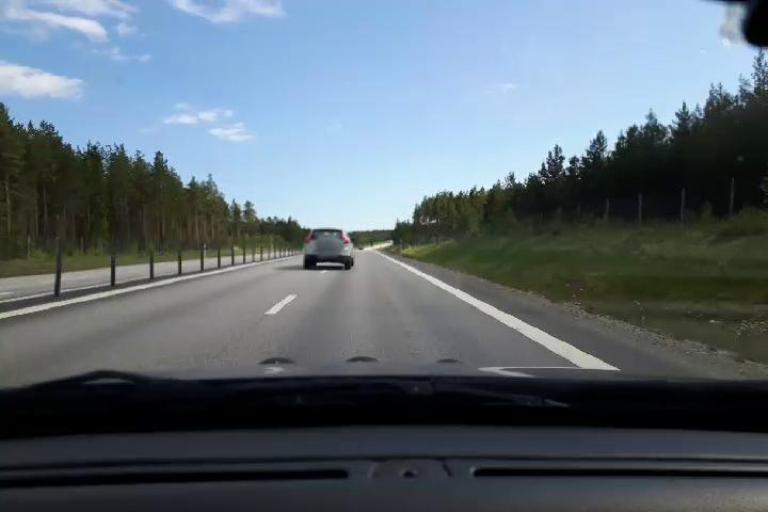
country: SE
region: Gaevleborg
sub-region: Hudiksvalls Kommun
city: Hudiksvall
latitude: 61.7040
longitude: 17.0524
